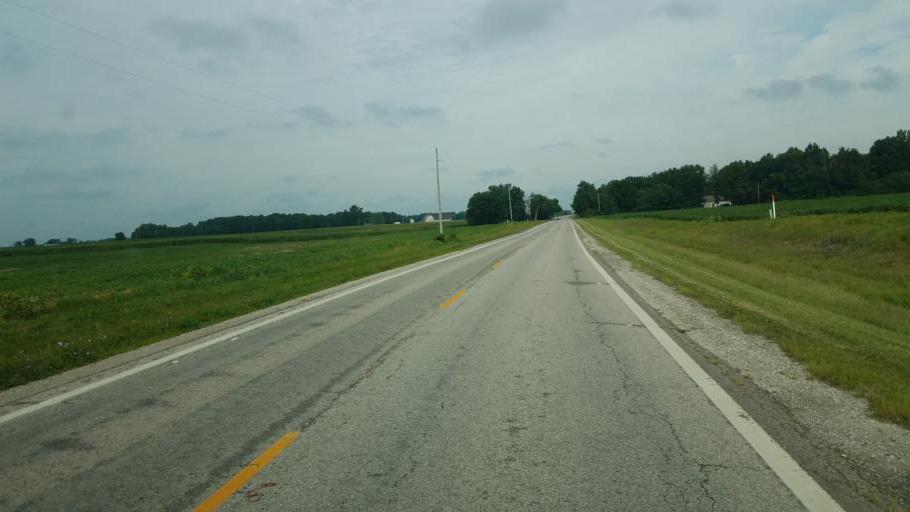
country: US
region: Ohio
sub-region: Morrow County
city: Cardington
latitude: 40.5174
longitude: -82.9404
